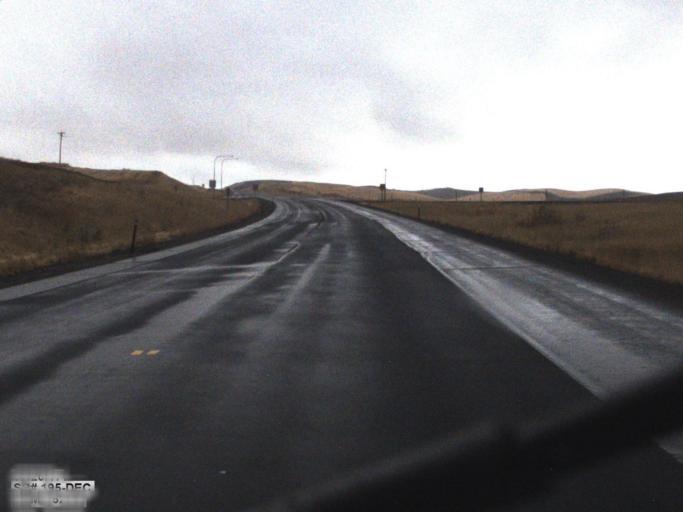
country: US
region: Washington
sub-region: Whitman County
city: Colfax
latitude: 47.2100
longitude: -117.3620
